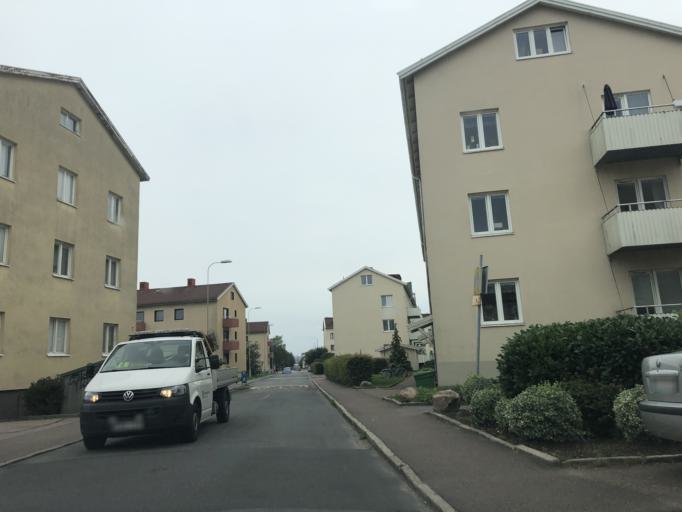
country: SE
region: Vaestra Goetaland
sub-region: Goteborg
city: Majorna
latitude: 57.7220
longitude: 11.9303
